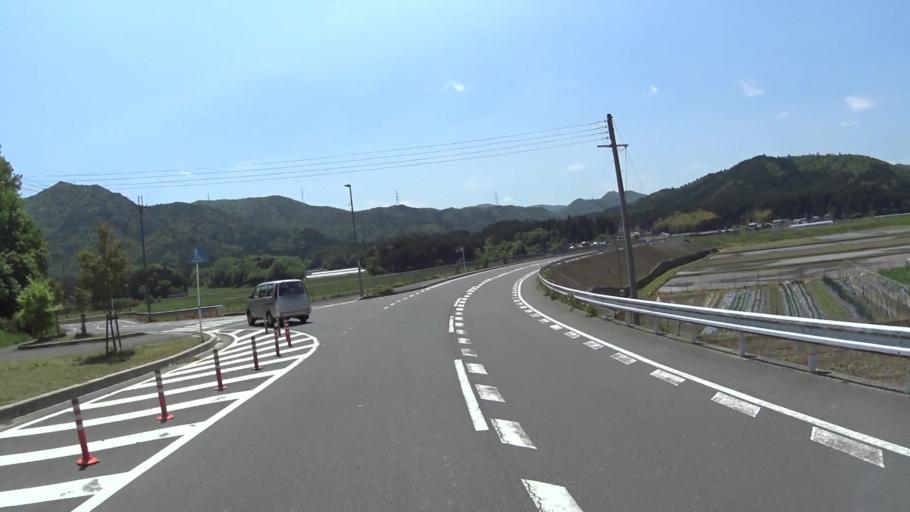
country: JP
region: Kyoto
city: Kameoka
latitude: 35.0628
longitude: 135.4575
